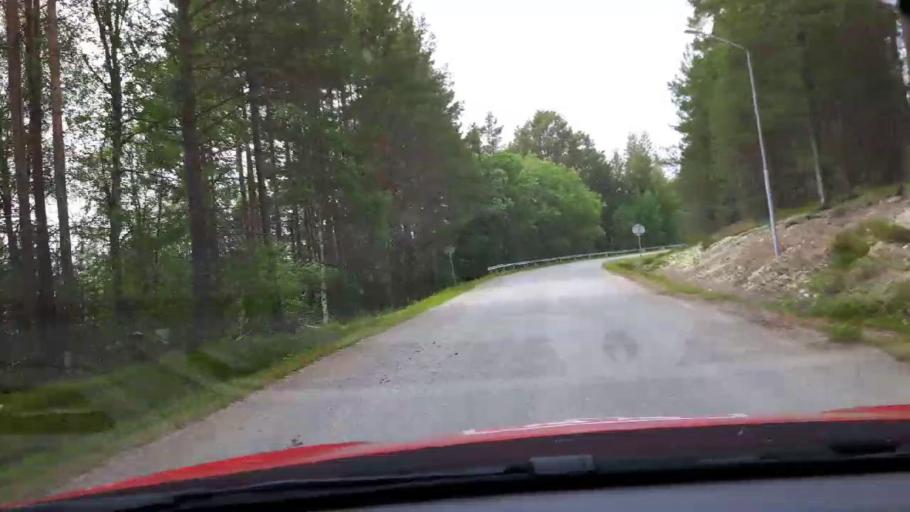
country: SE
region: Jaemtland
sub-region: Harjedalens Kommun
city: Sveg
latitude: 62.4119
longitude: 13.6620
